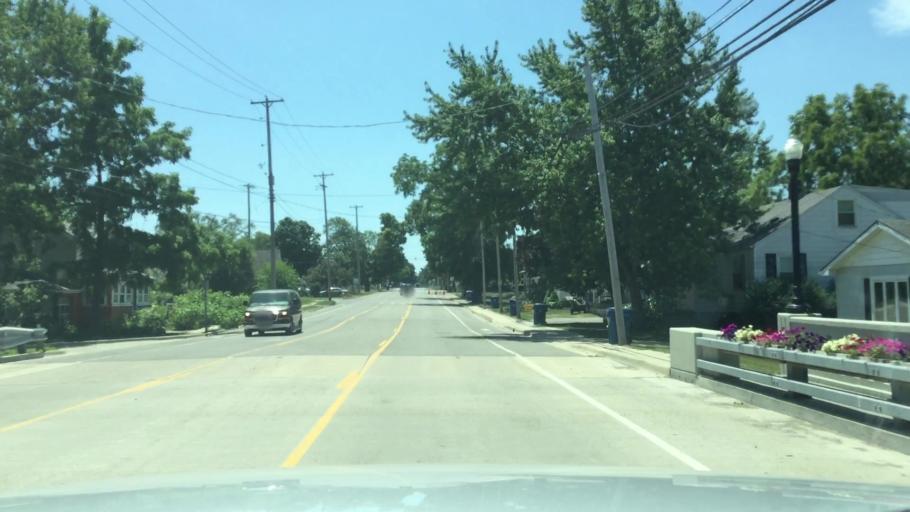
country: US
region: Michigan
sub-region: Genesee County
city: Swartz Creek
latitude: 42.9543
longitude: -83.8319
